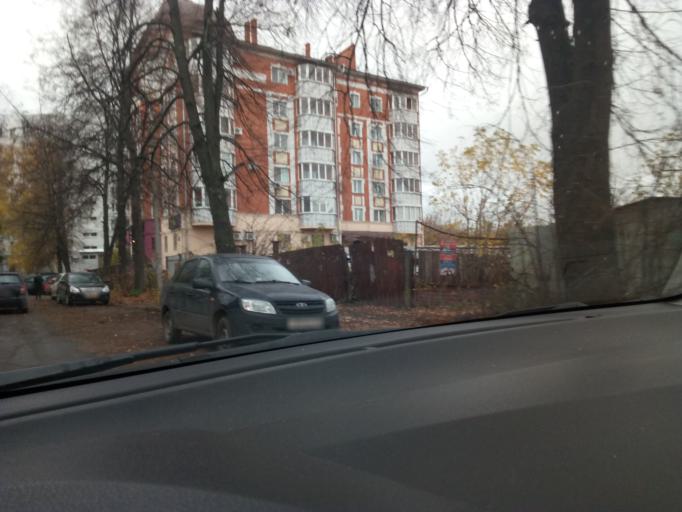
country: RU
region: Tatarstan
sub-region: Gorod Kazan'
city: Kazan
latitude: 55.7853
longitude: 49.1486
